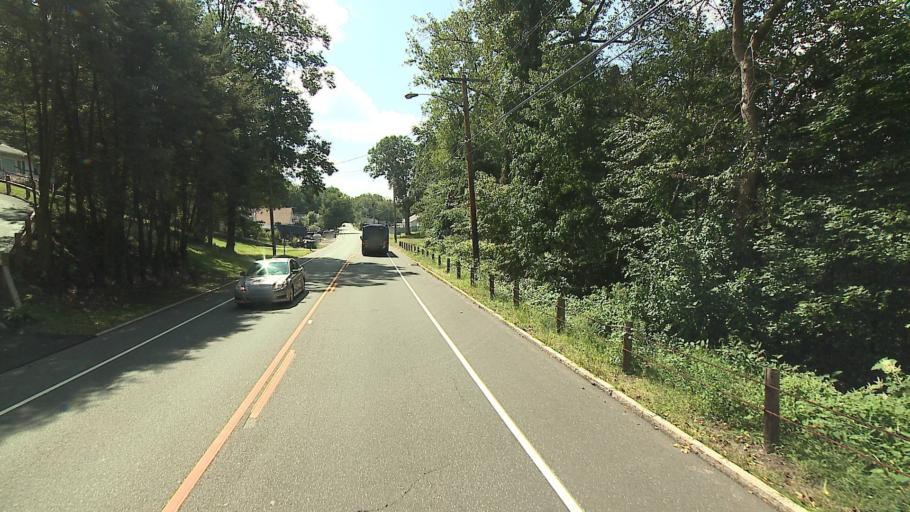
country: US
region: Connecticut
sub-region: New Haven County
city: Seymour
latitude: 41.3727
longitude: -73.0812
